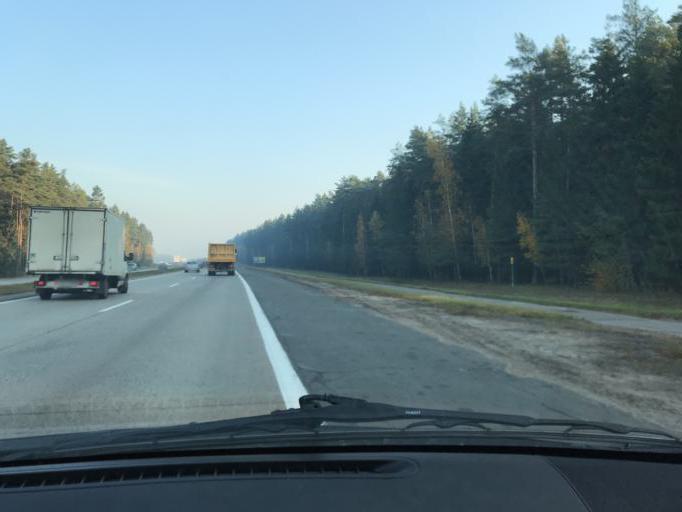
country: BY
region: Minsk
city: Borovlyany
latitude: 53.9841
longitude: 27.6559
